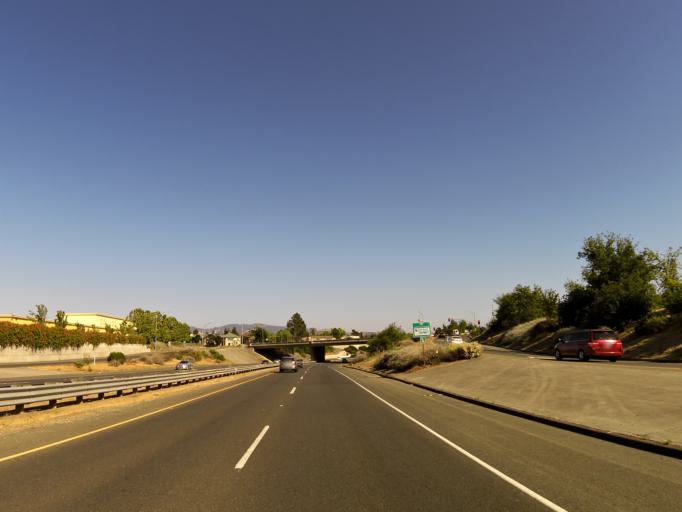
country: US
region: California
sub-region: Napa County
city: Napa
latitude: 38.3228
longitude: -122.3102
